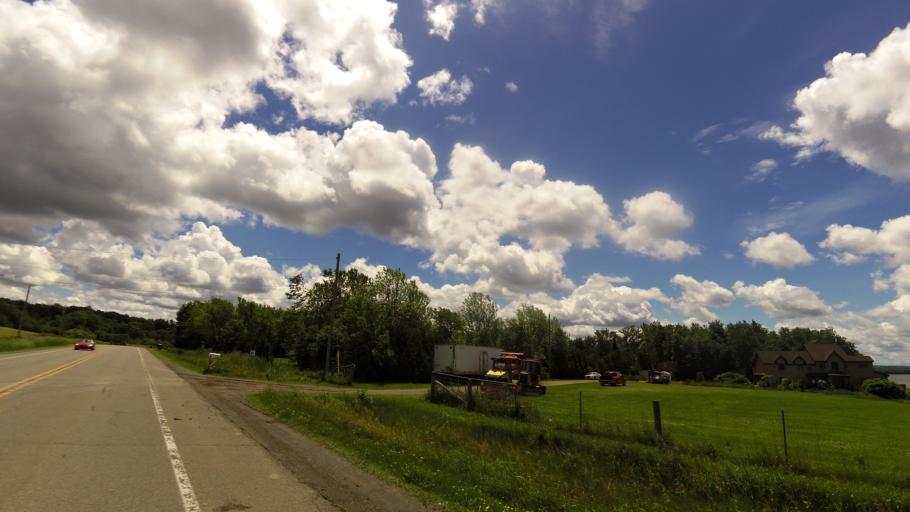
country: CA
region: Quebec
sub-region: Monteregie
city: Rigaud
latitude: 45.5358
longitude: -74.3072
